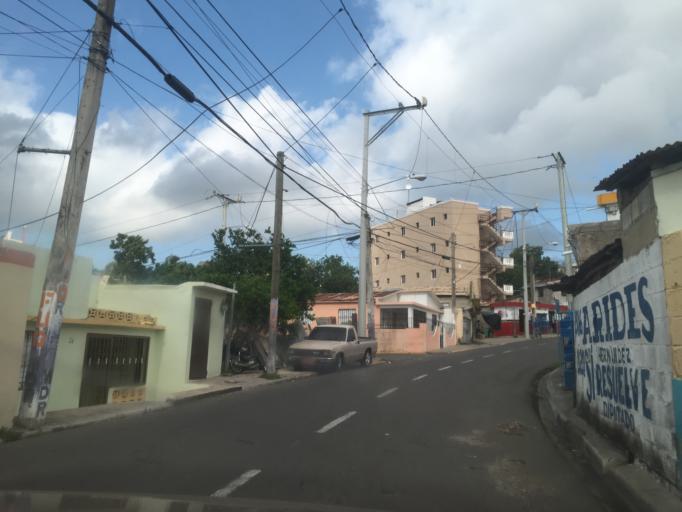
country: DO
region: Santiago
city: Santiago de los Caballeros
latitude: 19.4234
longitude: -70.7157
